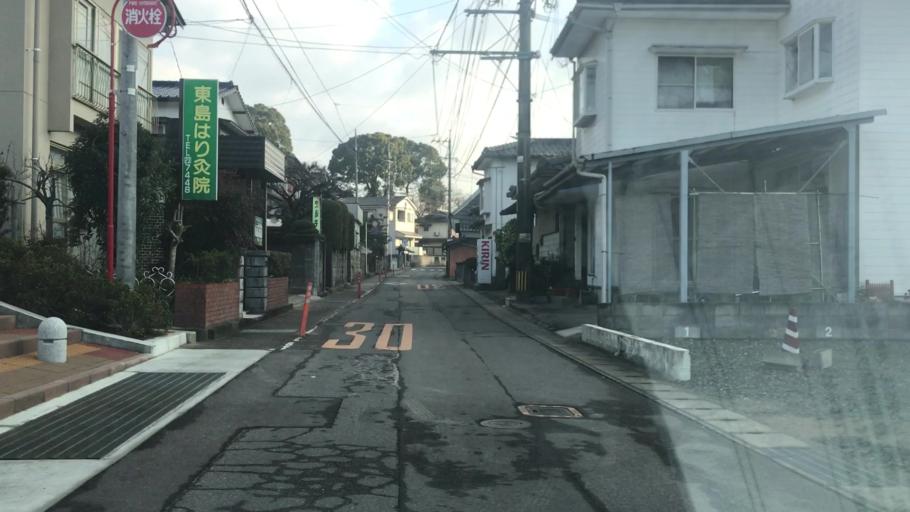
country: JP
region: Saga Prefecture
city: Takeocho-takeo
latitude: 33.1982
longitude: 130.0193
